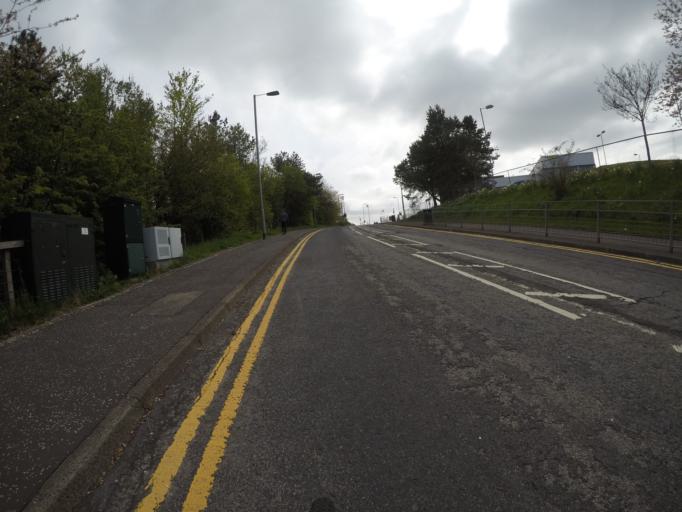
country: GB
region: Scotland
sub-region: East Renfrewshire
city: Newton Mearns
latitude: 55.7704
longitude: -4.3050
